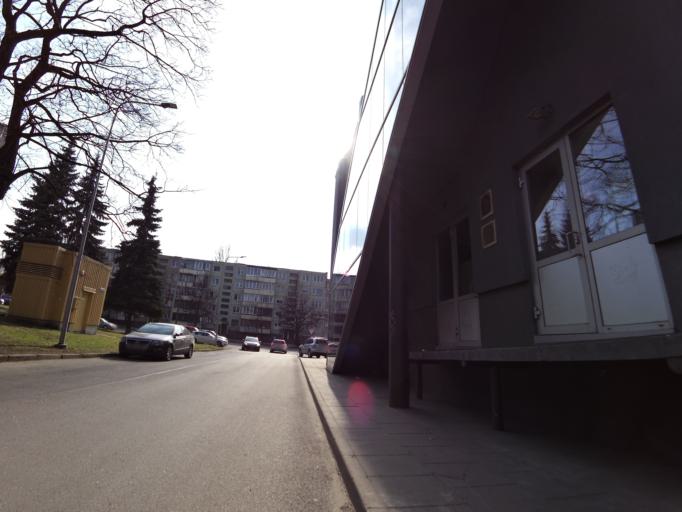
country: LT
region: Vilnius County
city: Vilkpede
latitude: 54.6748
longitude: 25.2533
